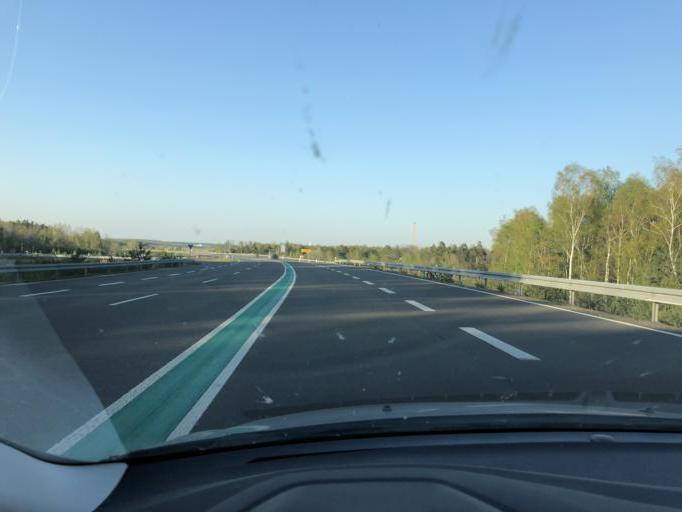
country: DE
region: Brandenburg
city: Senftenberg
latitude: 51.4994
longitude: 13.9549
